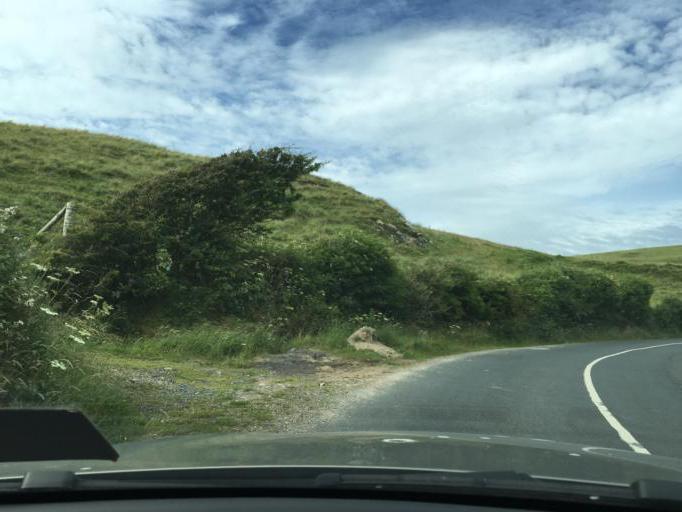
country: IE
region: Ulster
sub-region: County Donegal
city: Carndonagh
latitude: 55.3228
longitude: -7.3205
